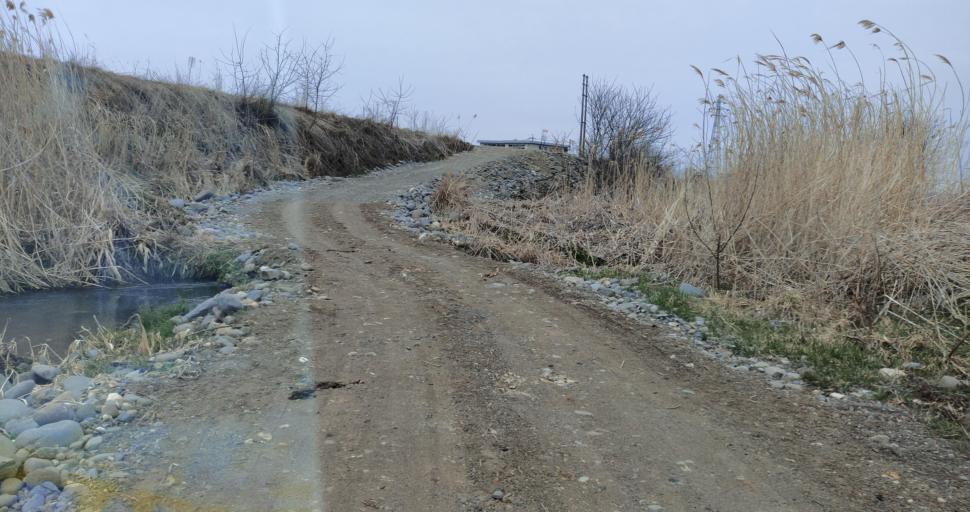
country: JP
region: Nagano
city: Saku
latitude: 36.2300
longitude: 138.4698
